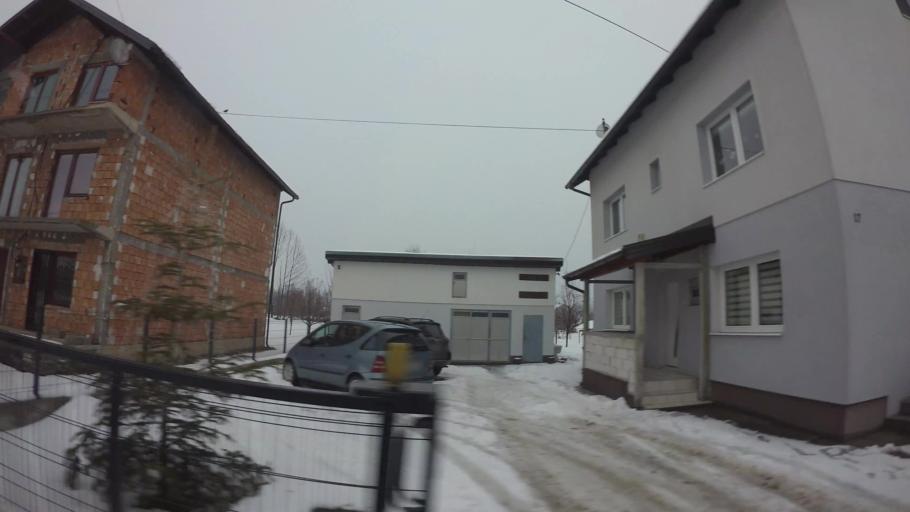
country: BA
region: Federation of Bosnia and Herzegovina
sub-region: Kanton Sarajevo
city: Sarajevo
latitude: 43.8430
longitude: 18.3015
